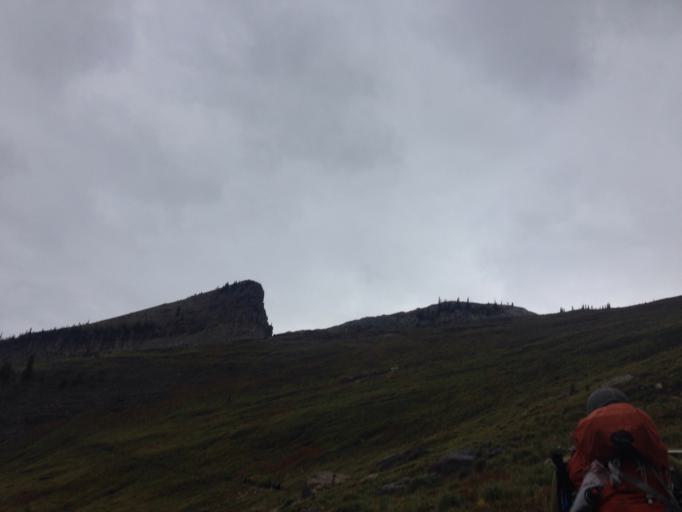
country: US
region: Montana
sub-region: Flathead County
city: Columbia Falls
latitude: 48.7345
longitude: -113.7236
